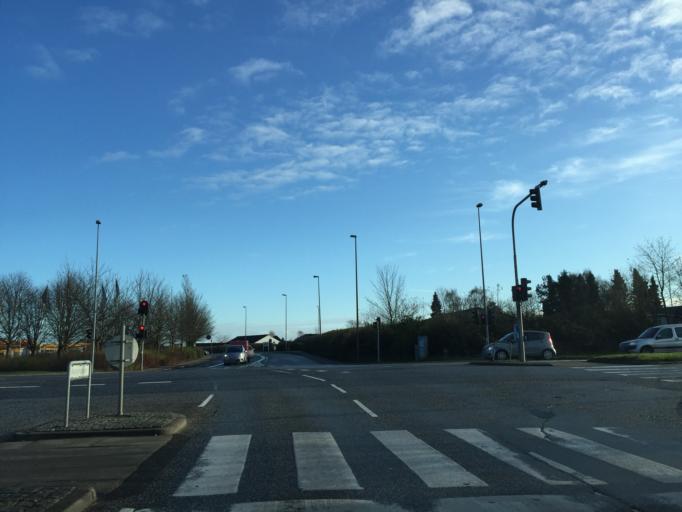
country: DK
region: Central Jutland
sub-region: Arhus Kommune
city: Stavtrup
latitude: 56.1821
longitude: 10.1003
